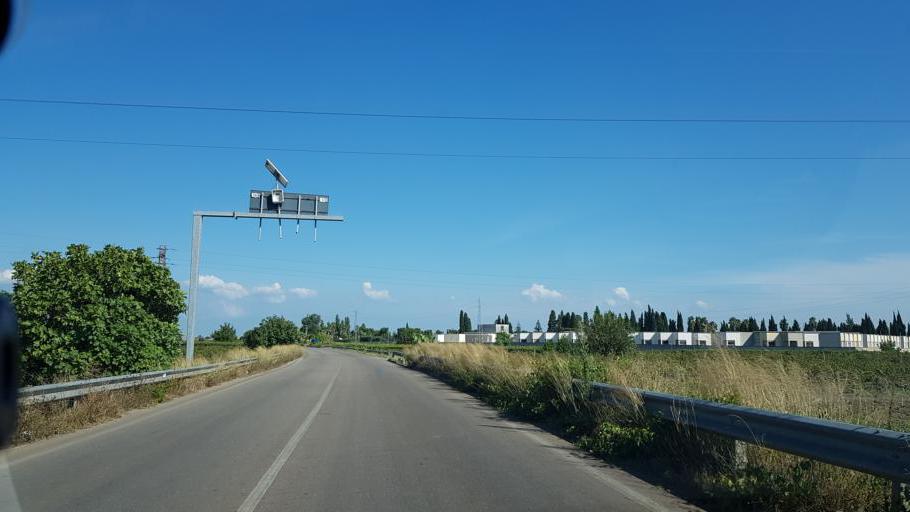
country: IT
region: Apulia
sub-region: Provincia di Lecce
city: Copertino
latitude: 40.2819
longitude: 18.0341
